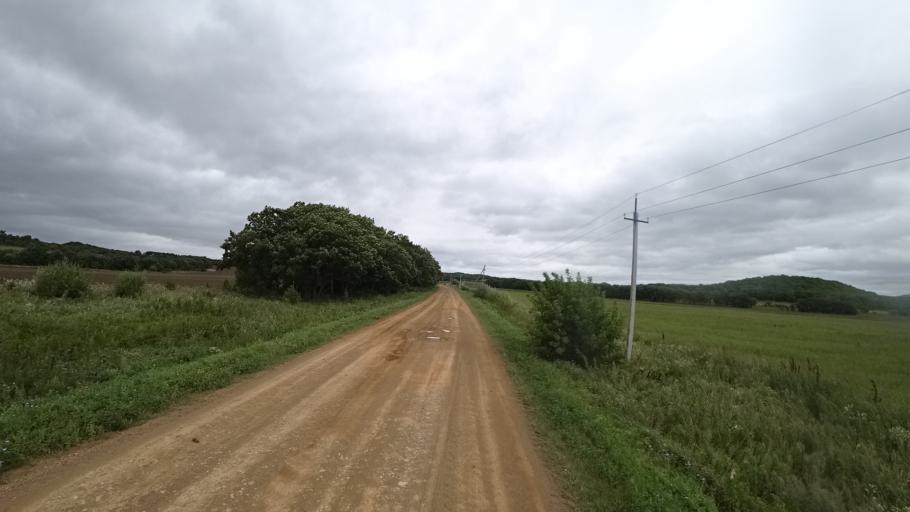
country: RU
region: Primorskiy
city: Chernigovka
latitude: 44.4426
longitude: 132.5951
